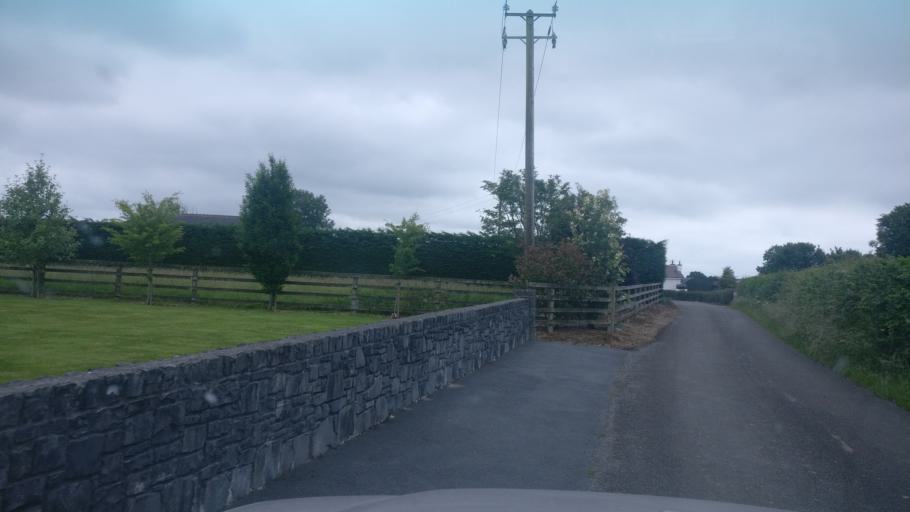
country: IE
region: Connaught
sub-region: County Galway
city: Ballinasloe
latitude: 53.2921
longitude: -8.3397
